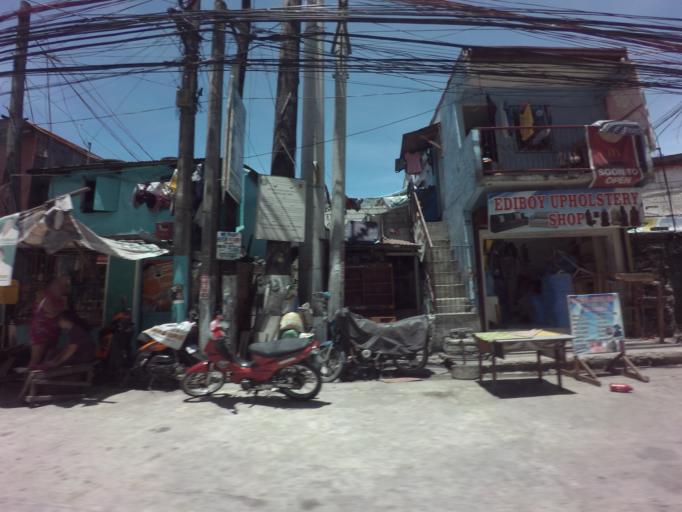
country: PH
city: Sambayanihan People's Village
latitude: 14.4879
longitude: 120.9863
